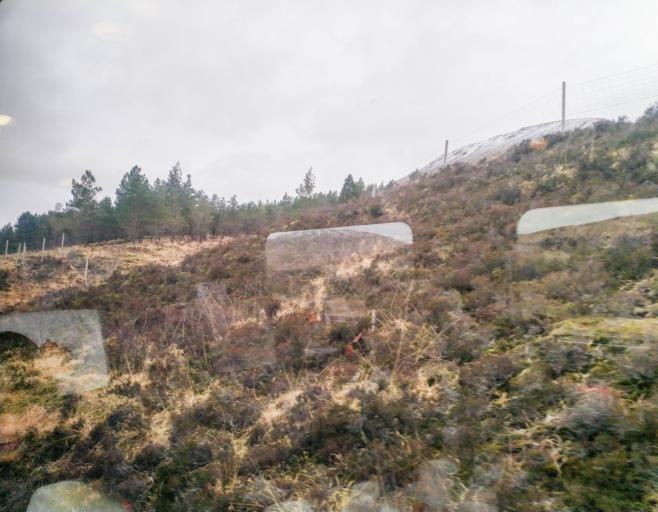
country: GB
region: Scotland
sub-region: Highland
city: Spean Bridge
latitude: 56.5221
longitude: -4.7637
